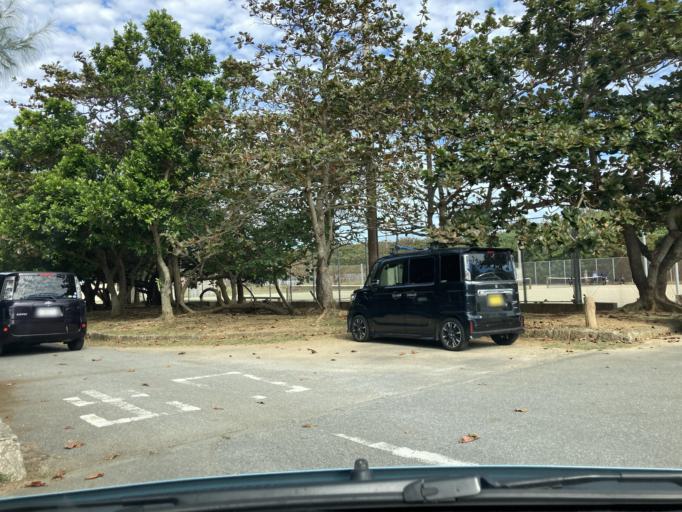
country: JP
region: Okinawa
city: Ishikawa
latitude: 26.4364
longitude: 127.7166
